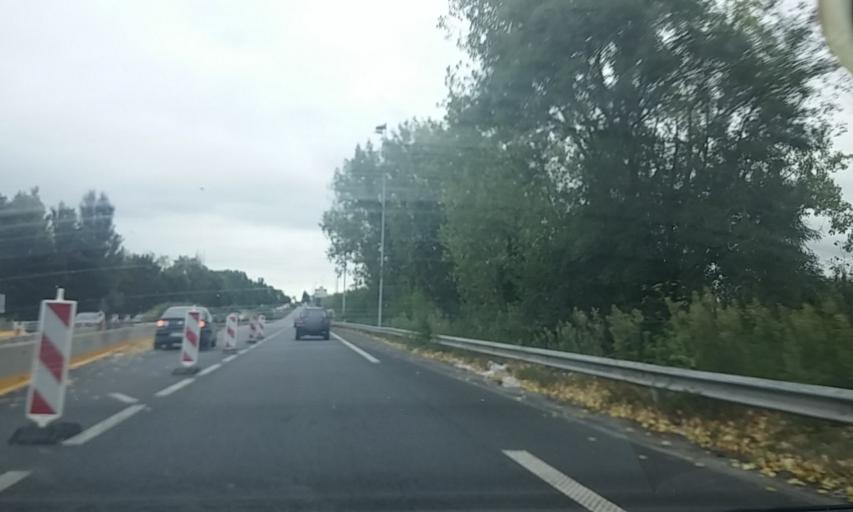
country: FR
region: Ile-de-France
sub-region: Departement du Val-de-Marne
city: Rungis
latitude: 48.7527
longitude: 2.3534
